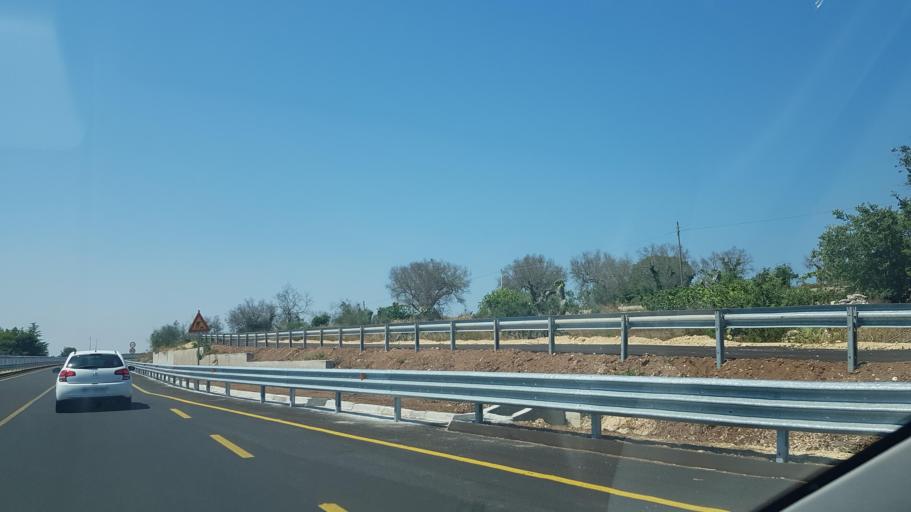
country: IT
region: Apulia
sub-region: Provincia di Lecce
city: Struda
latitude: 40.3170
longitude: 18.2749
